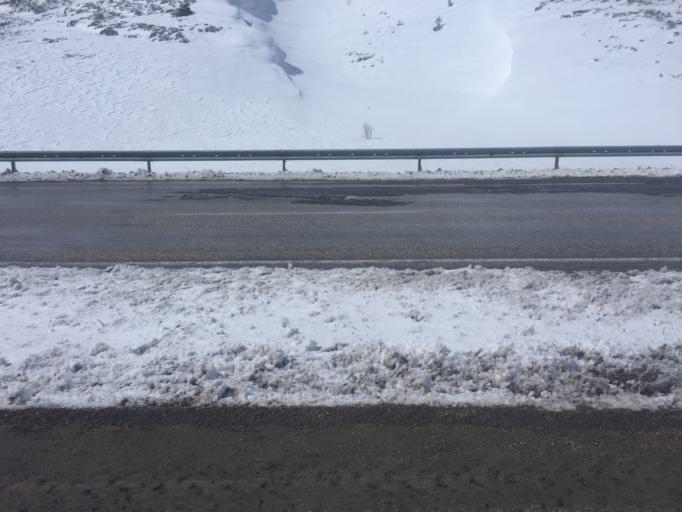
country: TR
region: Kahramanmaras
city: Goksun
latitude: 38.1951
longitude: 36.4565
